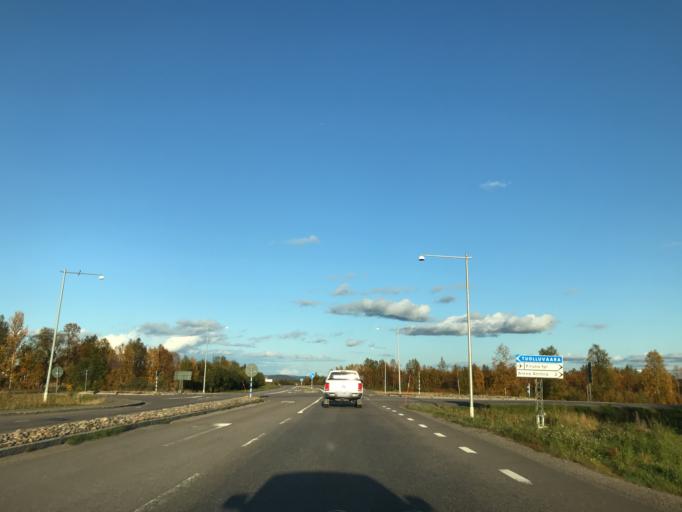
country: SE
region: Norrbotten
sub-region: Kiruna Kommun
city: Kiruna
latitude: 67.8456
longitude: 20.3474
